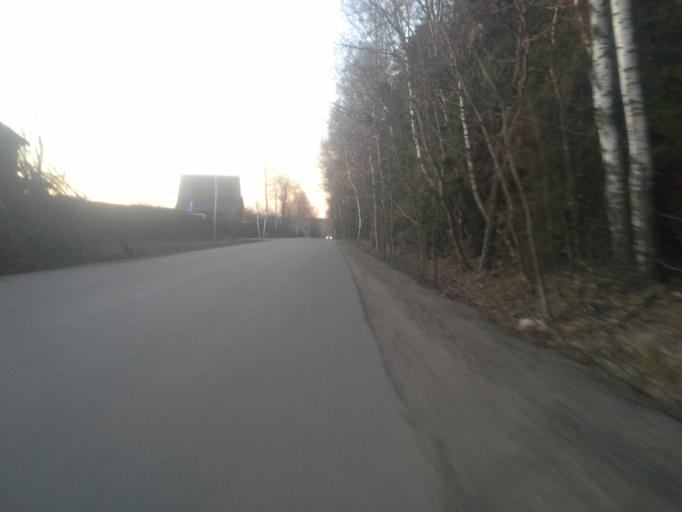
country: RU
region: Moscow
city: Tolstopal'tsevo
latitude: 55.6094
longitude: 37.2360
